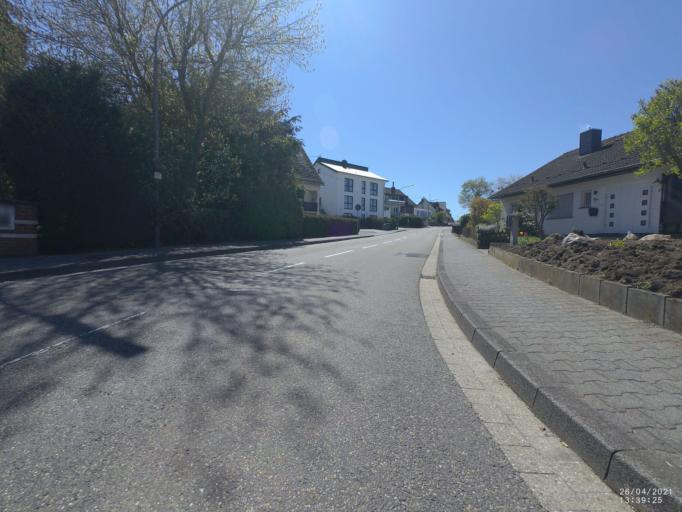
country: DE
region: Rheinland-Pfalz
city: Vallendar
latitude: 50.3975
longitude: 7.6254
